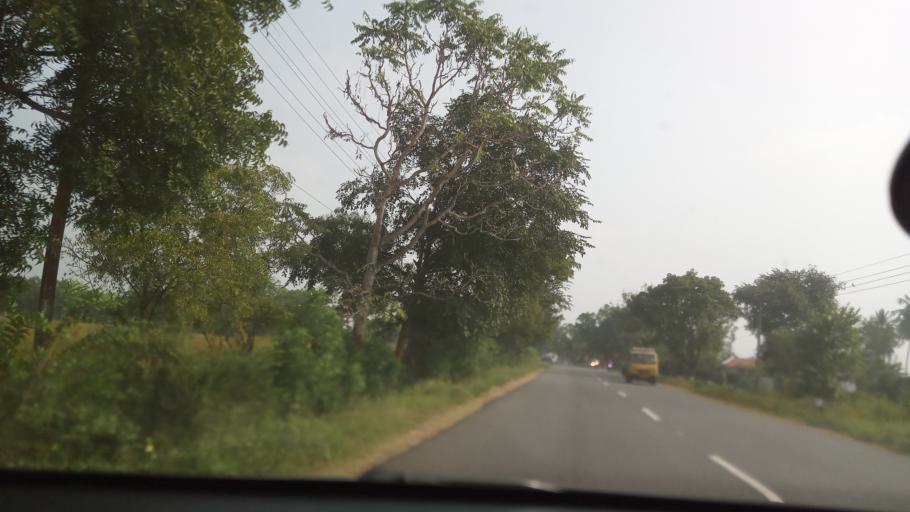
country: IN
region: Tamil Nadu
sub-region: Erode
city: Punjai Puliyampatti
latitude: 11.3300
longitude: 77.1521
